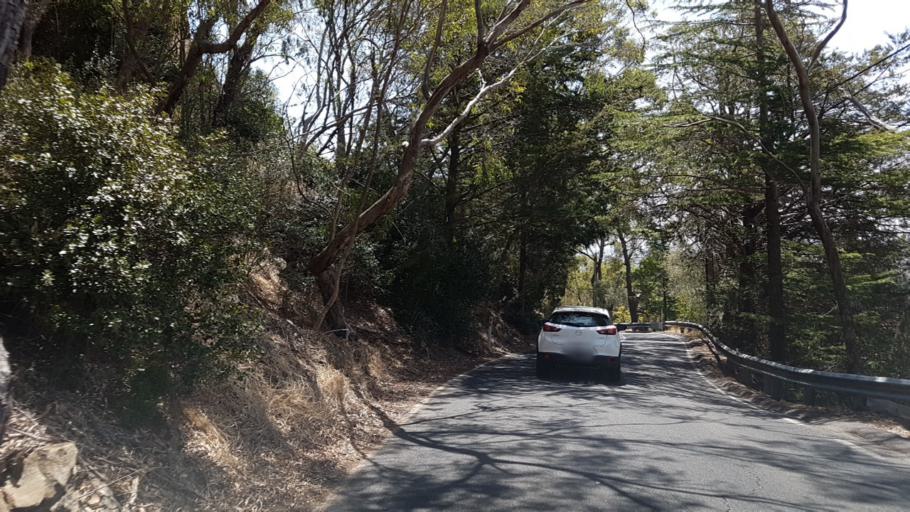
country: AU
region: South Australia
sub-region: Mitcham
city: Belair
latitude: -34.9943
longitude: 138.6284
